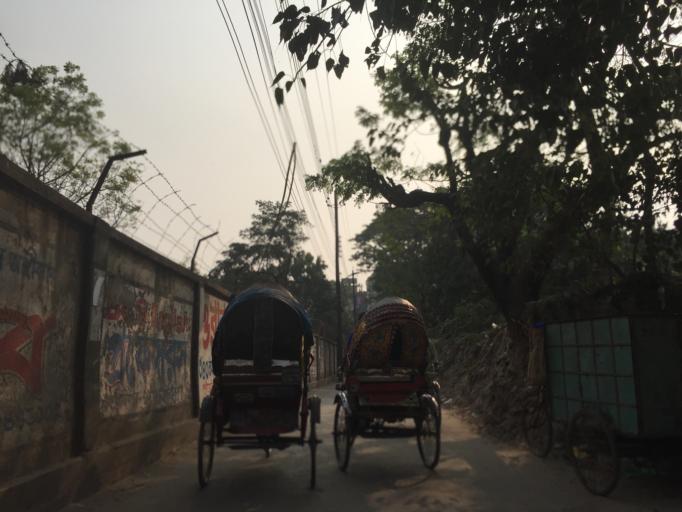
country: BD
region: Dhaka
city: Azimpur
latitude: 23.7295
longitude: 90.3815
